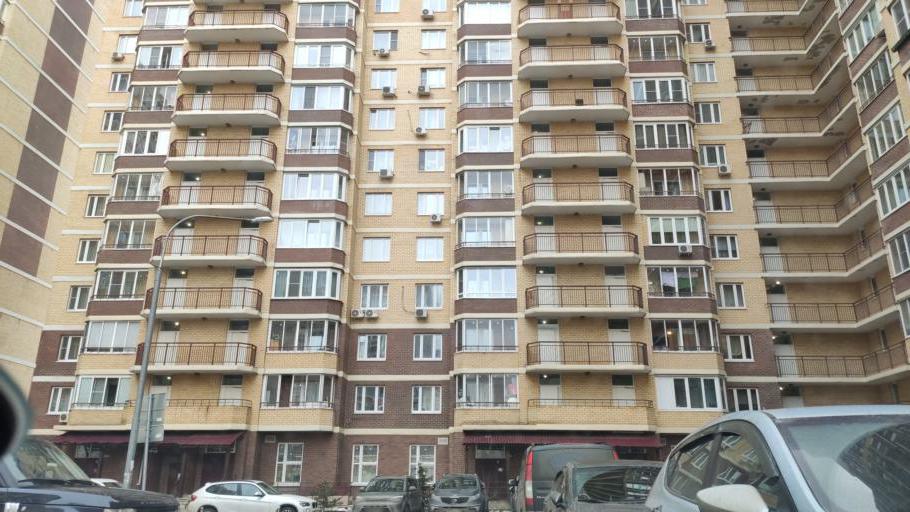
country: RU
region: Moskovskaya
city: Kommunarka
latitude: 55.5239
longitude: 37.5138
